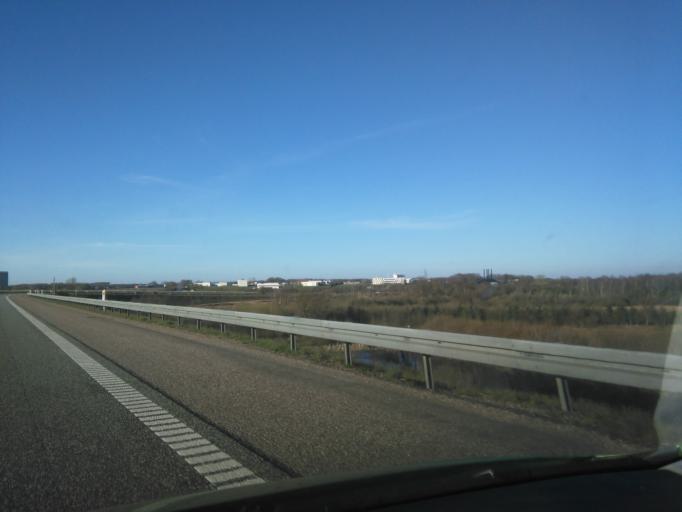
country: DK
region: Central Jutland
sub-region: Herning Kommune
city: Lind
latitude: 56.1216
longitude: 9.0123
